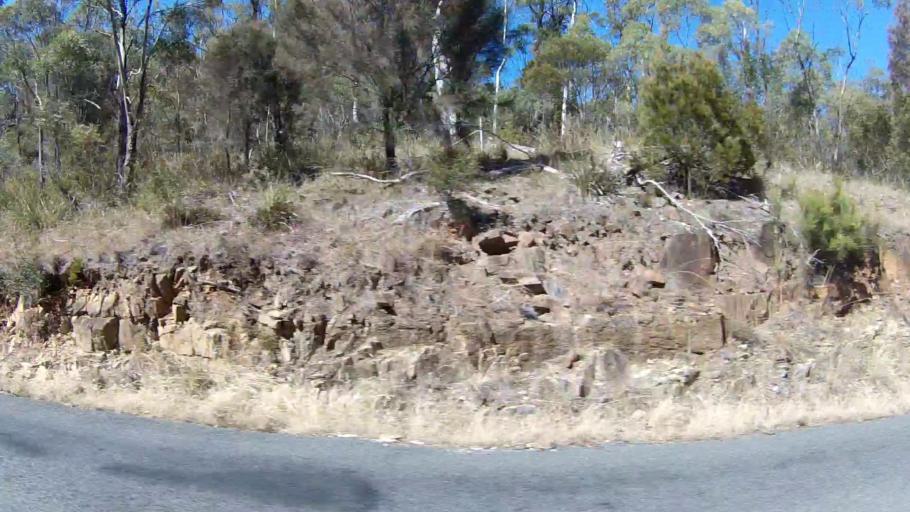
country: AU
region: Tasmania
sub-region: Sorell
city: Sorell
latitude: -42.5604
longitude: 147.8255
